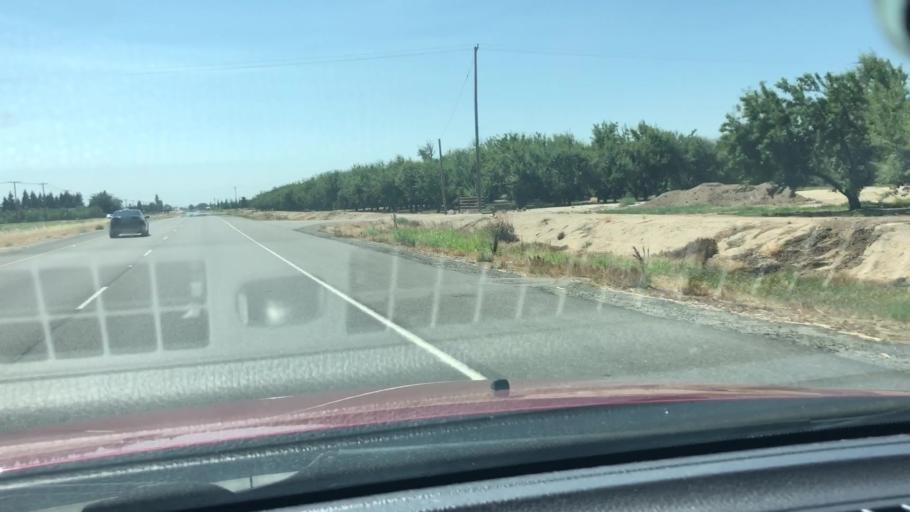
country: US
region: California
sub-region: Stanislaus County
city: Salida
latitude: 37.7119
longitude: -121.0541
